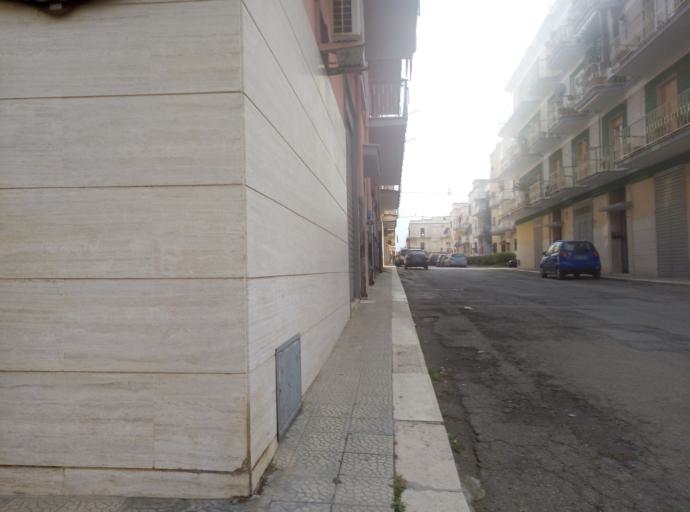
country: IT
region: Apulia
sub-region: Provincia di Bari
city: Ruvo di Puglia
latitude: 41.1221
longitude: 16.4860
